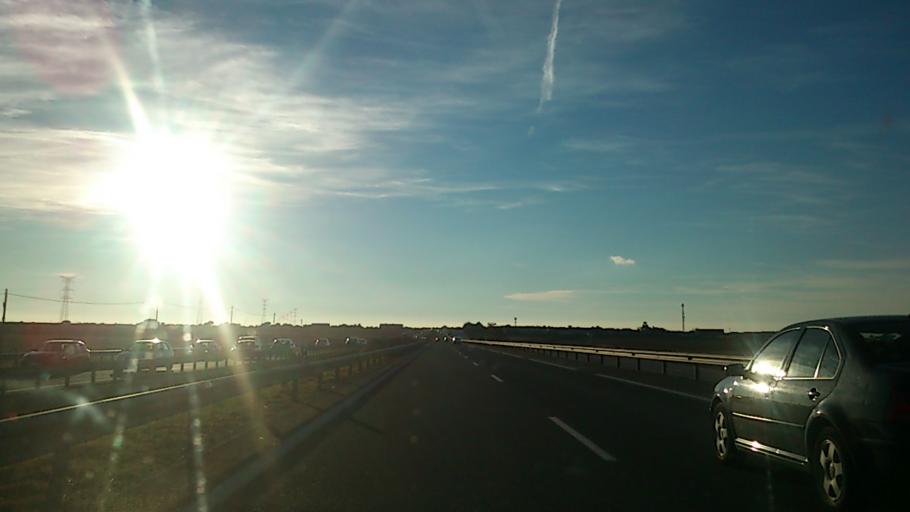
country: ES
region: Castille-La Mancha
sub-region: Provincia de Guadalajara
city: Gajanejos
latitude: 40.8444
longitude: -2.8786
